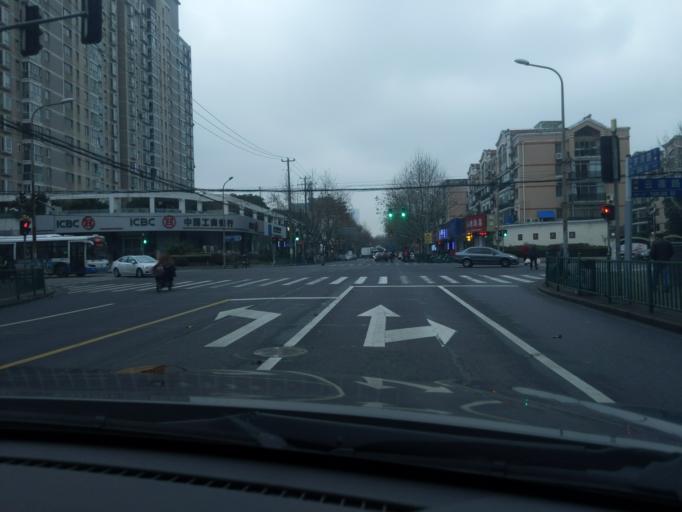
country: CN
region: Shanghai Shi
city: Luwan
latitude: 31.1821
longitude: 121.5018
